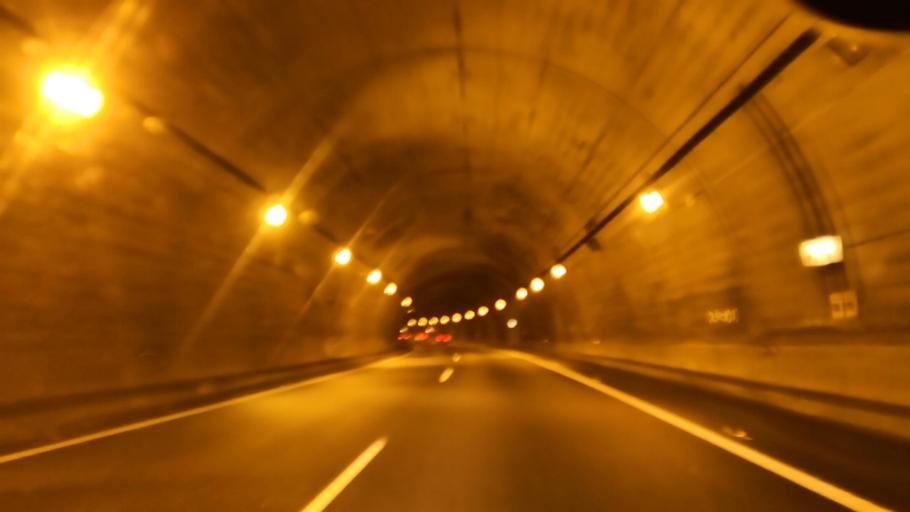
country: ES
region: Galicia
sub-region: Provincia de Pontevedra
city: Vigo
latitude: 42.2406
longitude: -8.6668
